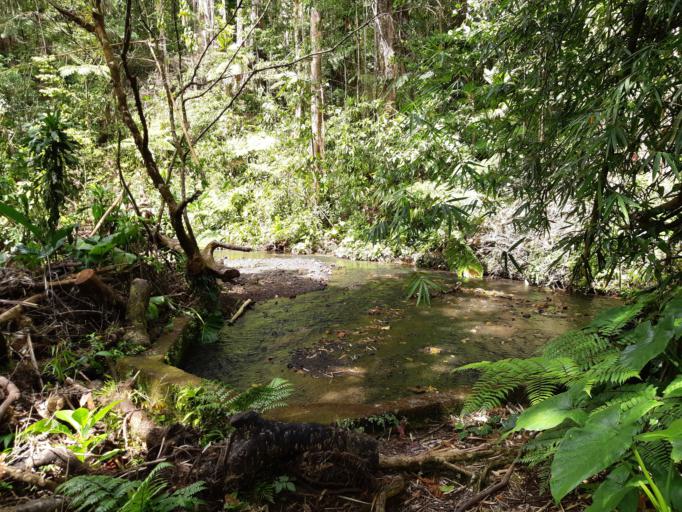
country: GP
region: Guadeloupe
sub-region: Guadeloupe
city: Saint-Claude
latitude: 16.0324
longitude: -61.6781
